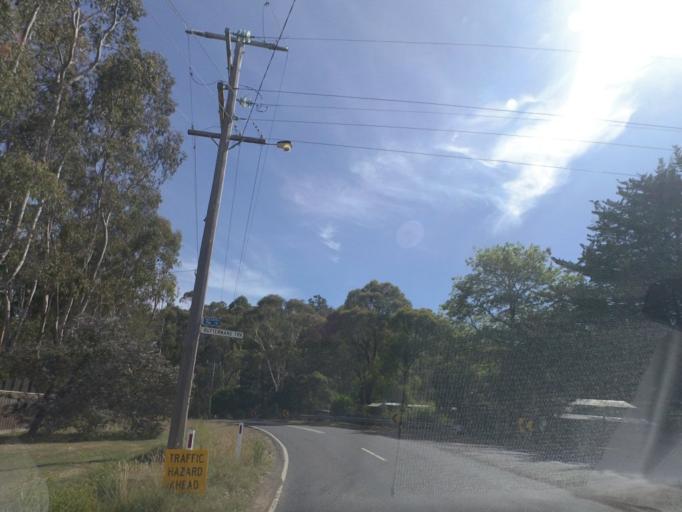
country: AU
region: Victoria
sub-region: Nillumbik
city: Saint Andrews
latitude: -37.5952
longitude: 145.2815
